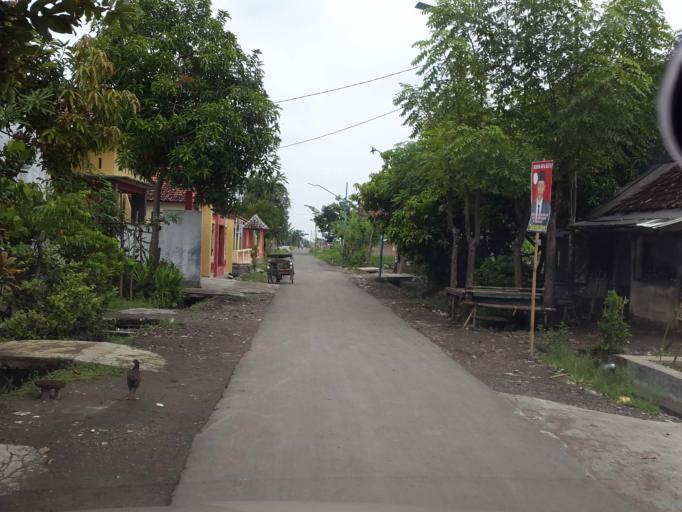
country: ID
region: Central Java
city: Dukuhturi
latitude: -6.8800
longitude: 109.0301
